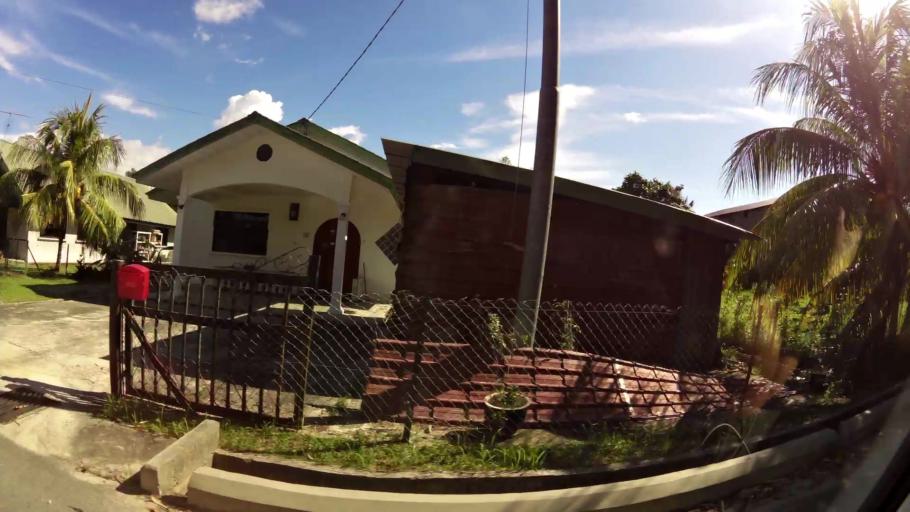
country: BN
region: Brunei and Muara
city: Bandar Seri Begawan
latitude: 4.9627
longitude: 114.9332
